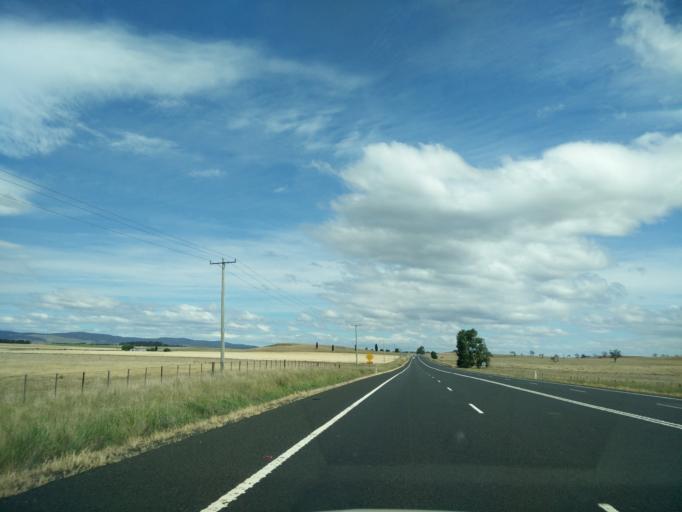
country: AU
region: Tasmania
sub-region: Northern Midlands
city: Evandale
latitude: -41.8715
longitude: 147.4605
